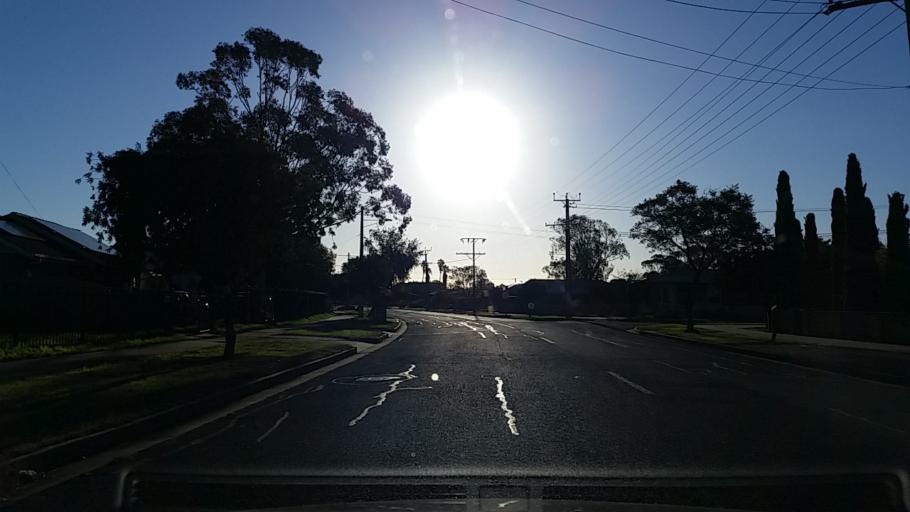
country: AU
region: South Australia
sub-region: Playford
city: Smithfield
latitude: -34.6826
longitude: 138.6683
